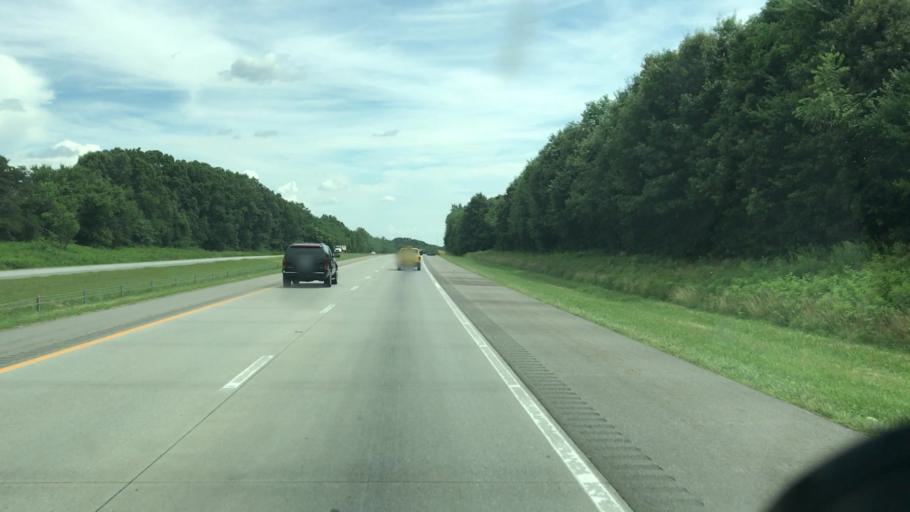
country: US
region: North Carolina
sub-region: Yadkin County
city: Jonesville
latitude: 36.1486
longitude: -80.8082
